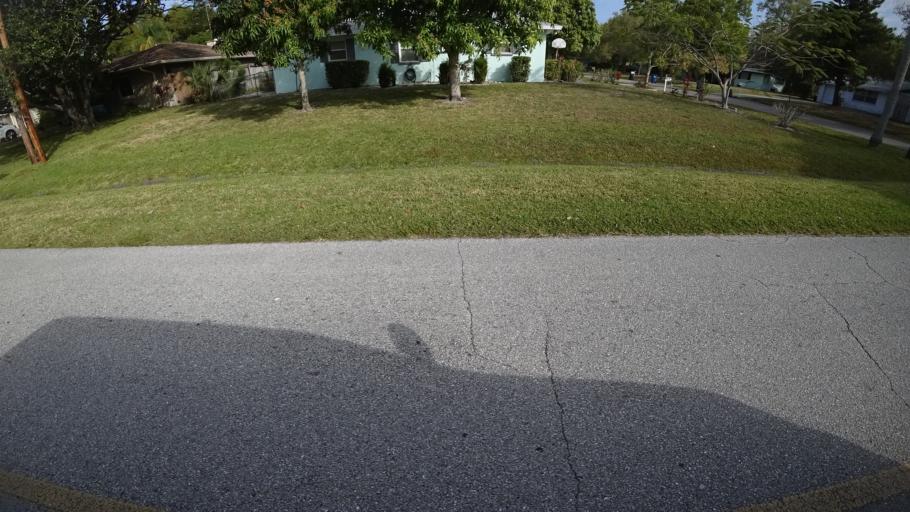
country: US
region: Florida
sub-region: Manatee County
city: Whitfield
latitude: 27.4221
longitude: -82.5533
